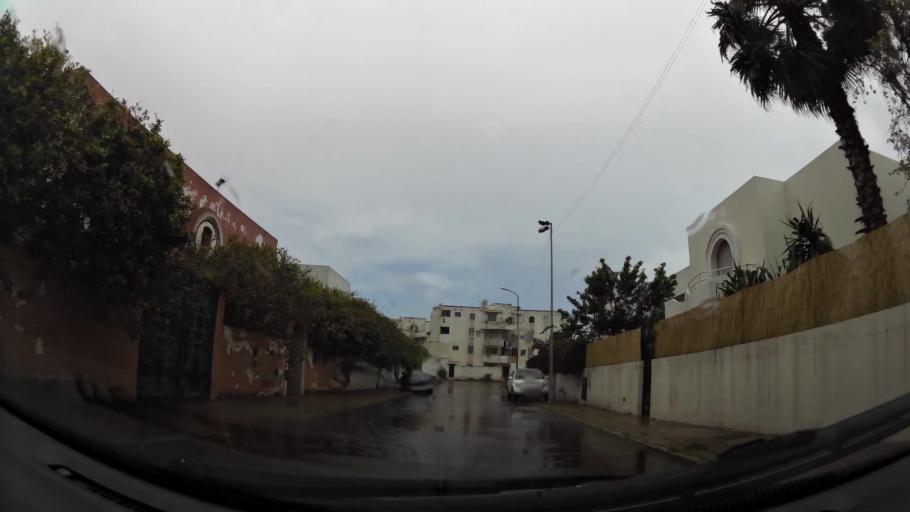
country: MA
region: Grand Casablanca
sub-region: Casablanca
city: Casablanca
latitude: 33.5716
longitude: -7.6329
